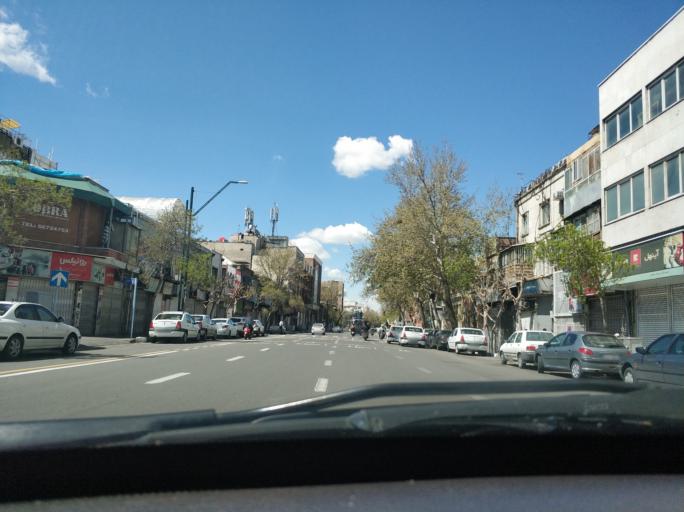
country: IR
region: Tehran
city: Tehran
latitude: 35.6859
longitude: 51.4133
